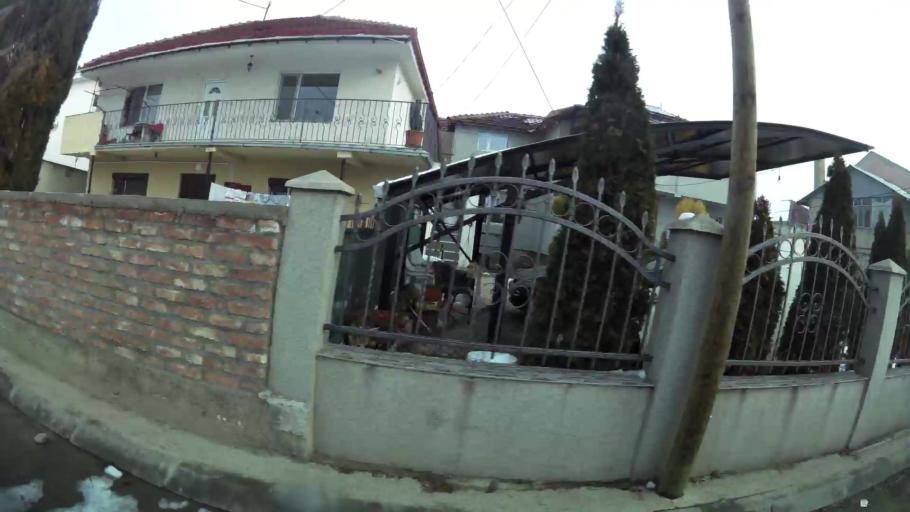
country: MK
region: Saraj
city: Saraj
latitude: 42.0246
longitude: 21.3526
